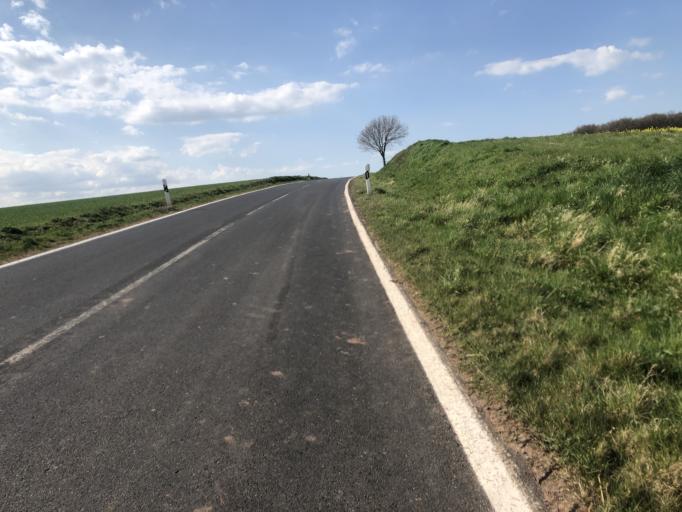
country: DE
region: North Rhine-Westphalia
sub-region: Regierungsbezirk Koln
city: Kall
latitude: 50.6081
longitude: 6.5773
